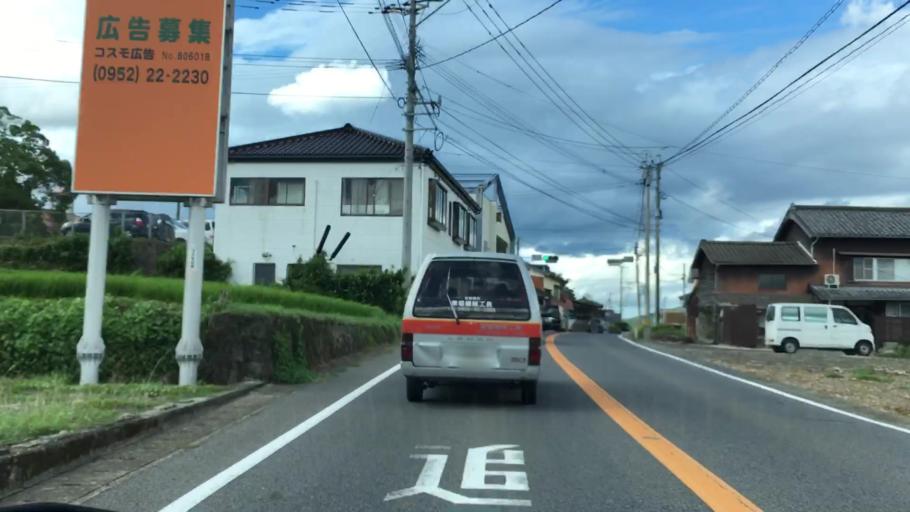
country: JP
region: Saga Prefecture
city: Imaricho-ko
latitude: 33.2045
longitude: 129.8501
